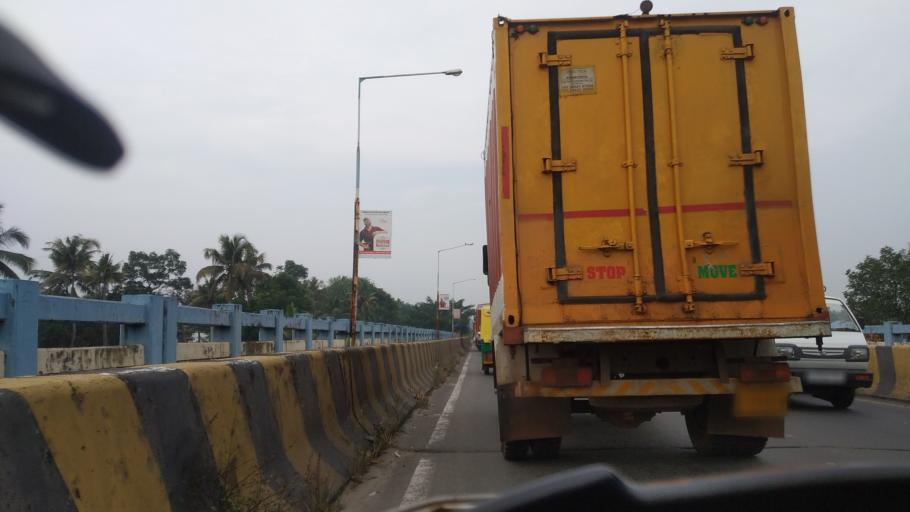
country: IN
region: Kerala
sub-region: Ernakulam
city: Elur
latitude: 10.0376
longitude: 76.3019
